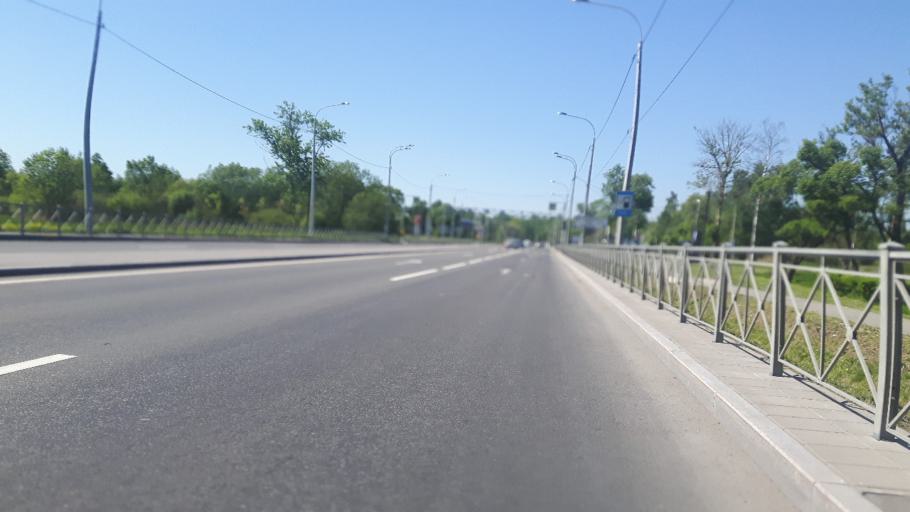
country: RU
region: Leningrad
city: Gorbunki
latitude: 59.8685
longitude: 29.9756
